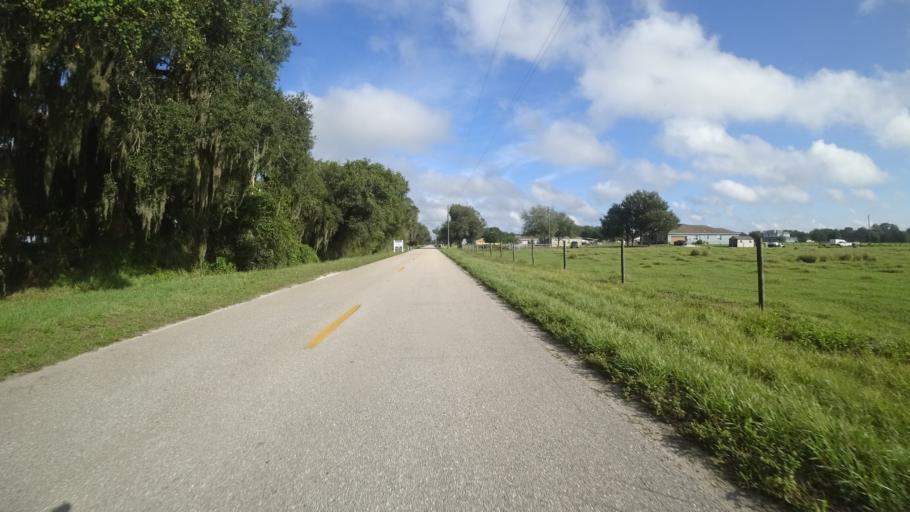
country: US
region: Florida
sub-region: Manatee County
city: Ellenton
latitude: 27.5680
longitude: -82.4090
